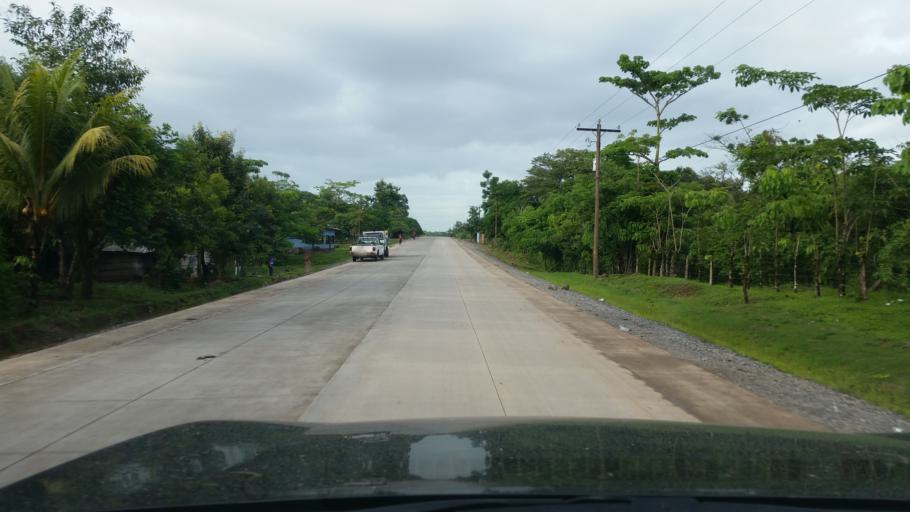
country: NI
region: Matagalpa
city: Rio Blanco
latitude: 13.1221
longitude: -85.0533
